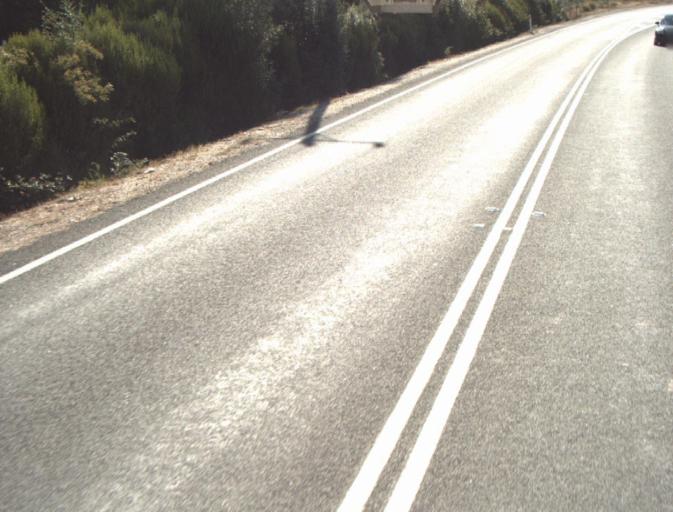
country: AU
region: Tasmania
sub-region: Launceston
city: Mayfield
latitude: -41.3613
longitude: 147.1436
